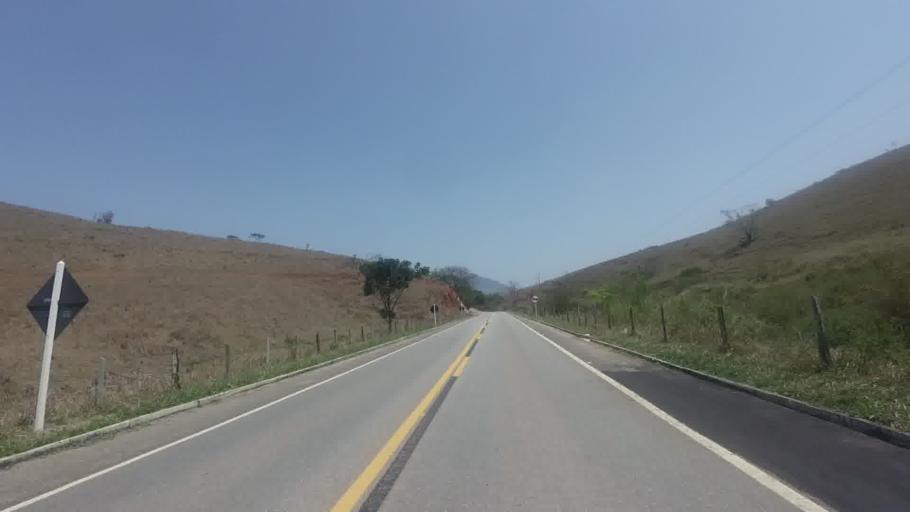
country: BR
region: Espirito Santo
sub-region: Jeronimo Monteiro
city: Jeronimo Monteiro
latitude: -20.8993
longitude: -41.2902
